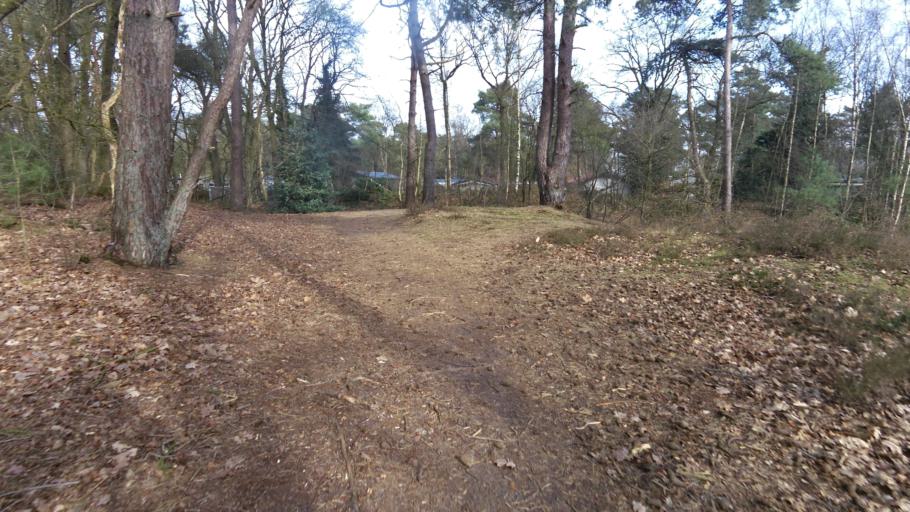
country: NL
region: Utrecht
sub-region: Gemeente Utrechtse Heuvelrug
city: Maarn
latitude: 52.0705
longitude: 5.3664
